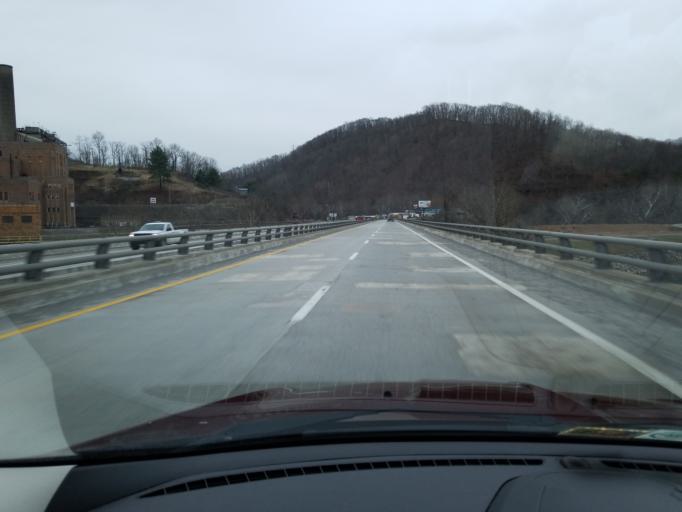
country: US
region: Virginia
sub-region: Giles County
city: Narrows
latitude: 37.3726
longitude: -80.8625
